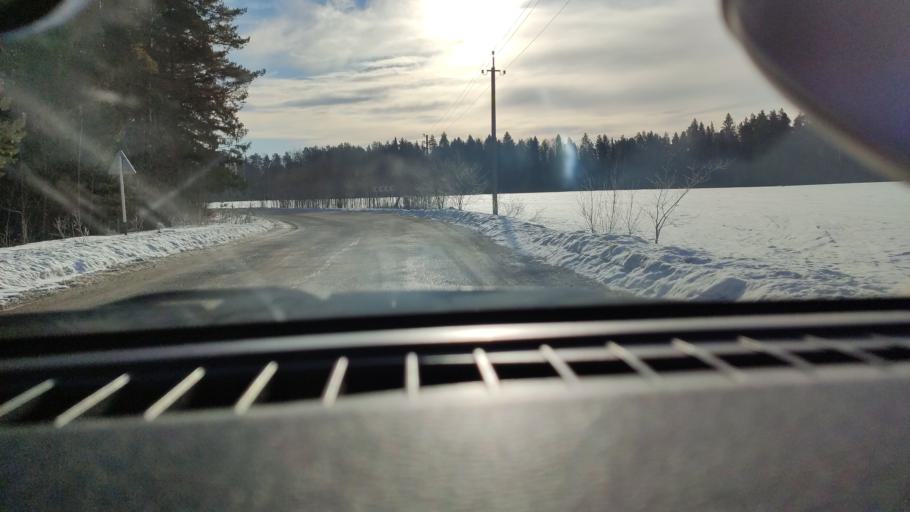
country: RU
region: Perm
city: Ust'-Kachka
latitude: 58.0041
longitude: 55.5906
